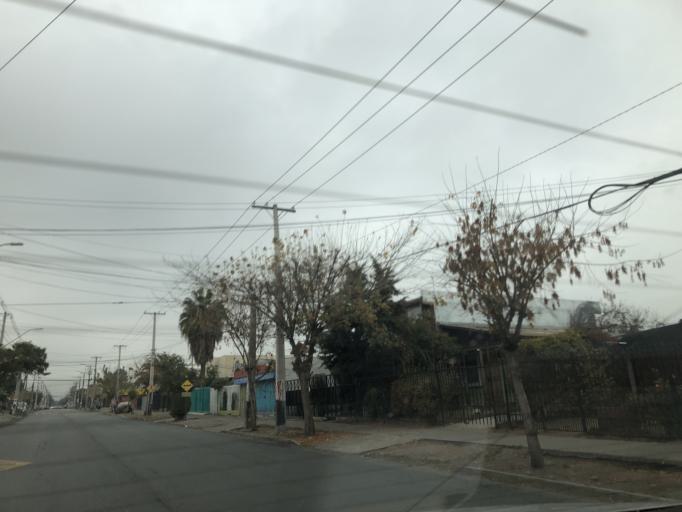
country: CL
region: Santiago Metropolitan
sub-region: Provincia de Cordillera
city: Puente Alto
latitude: -33.5875
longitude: -70.5955
